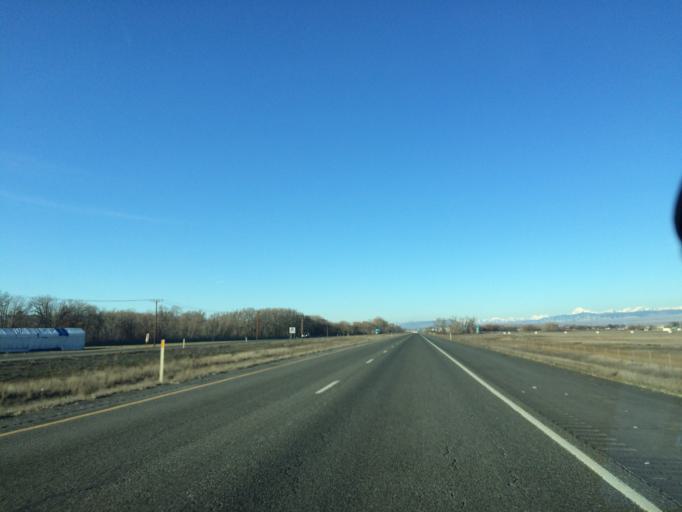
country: US
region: Washington
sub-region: Kittitas County
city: Ellensburg
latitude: 46.9837
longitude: -120.5634
